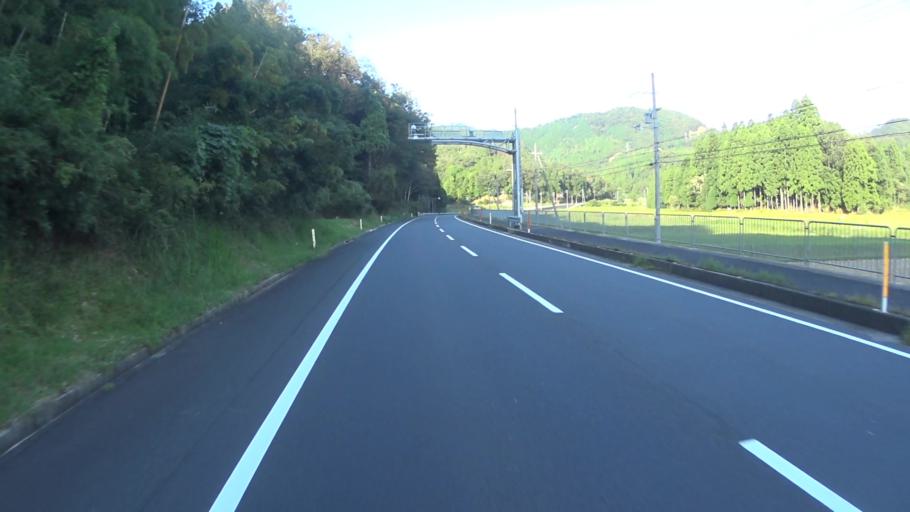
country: JP
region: Hyogo
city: Toyooka
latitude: 35.5743
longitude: 134.9848
